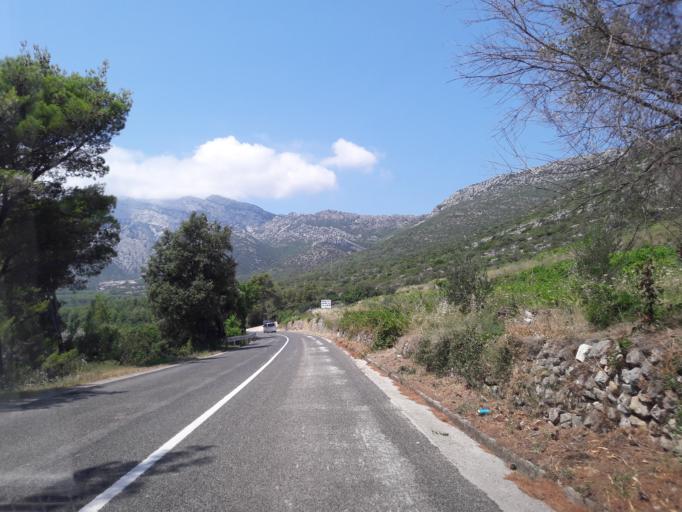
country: HR
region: Dubrovacko-Neretvanska
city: Orebic
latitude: 42.9803
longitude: 17.2206
